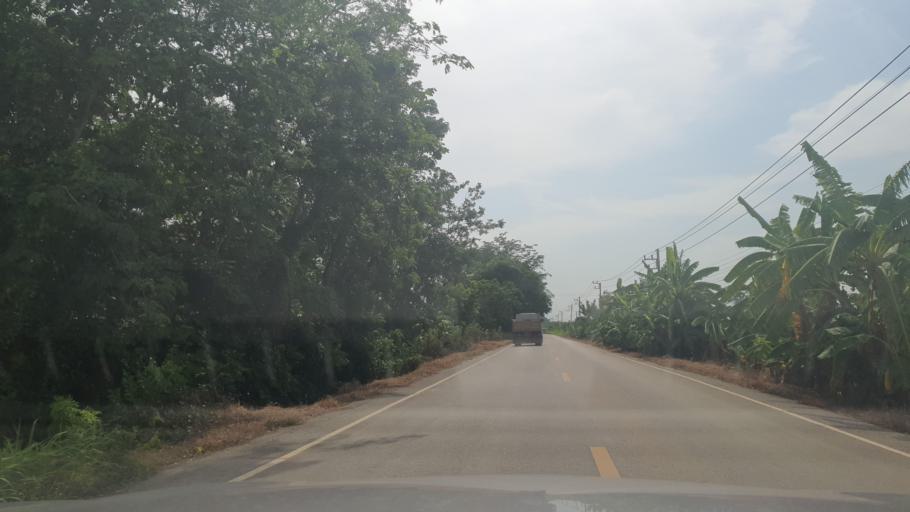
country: TH
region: Sukhothai
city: Si Samrong
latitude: 17.1173
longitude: 99.8758
